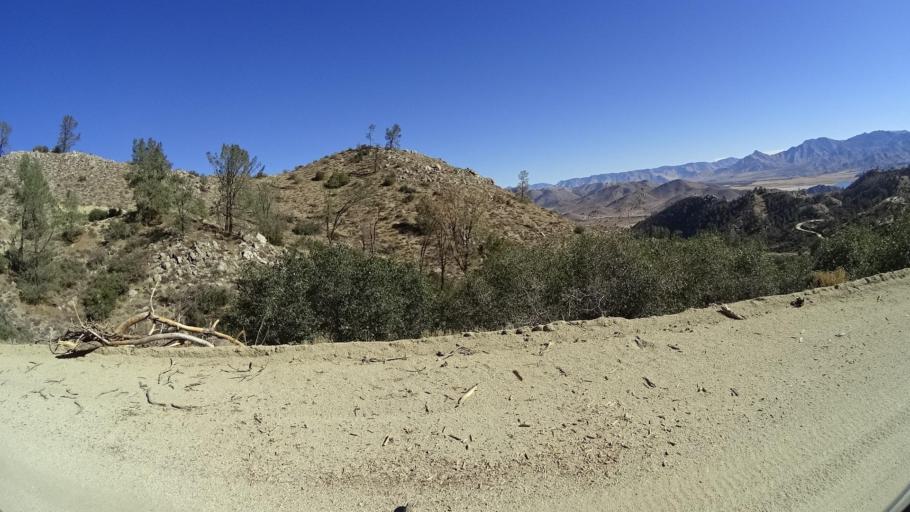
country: US
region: California
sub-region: Kern County
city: Wofford Heights
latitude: 35.7041
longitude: -118.4884
